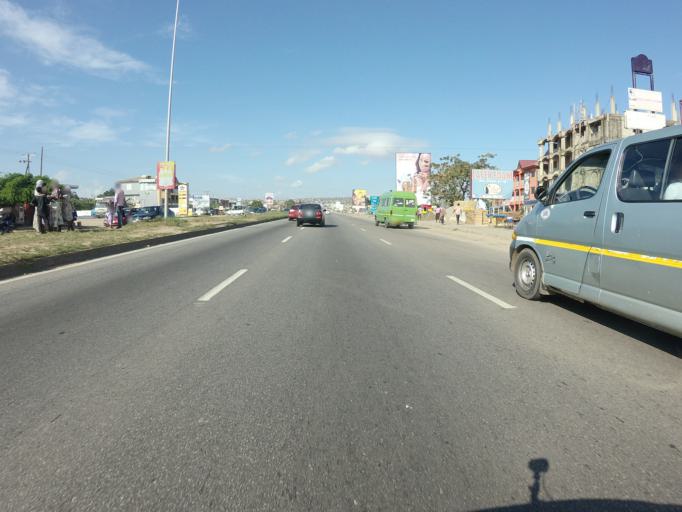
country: GH
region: Greater Accra
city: Gbawe
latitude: 5.5507
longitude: -0.3306
